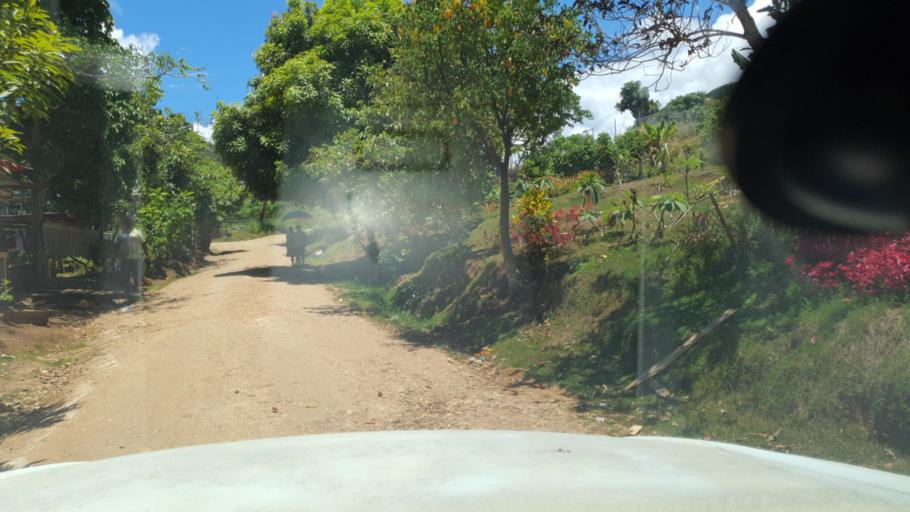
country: SB
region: Guadalcanal
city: Honiara
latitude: -9.4543
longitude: 159.9942
